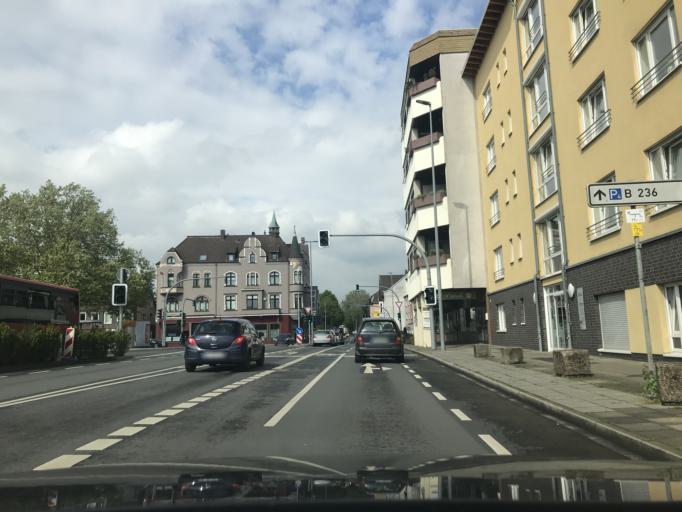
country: DE
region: North Rhine-Westphalia
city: Schwerte
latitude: 51.4413
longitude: 7.5605
